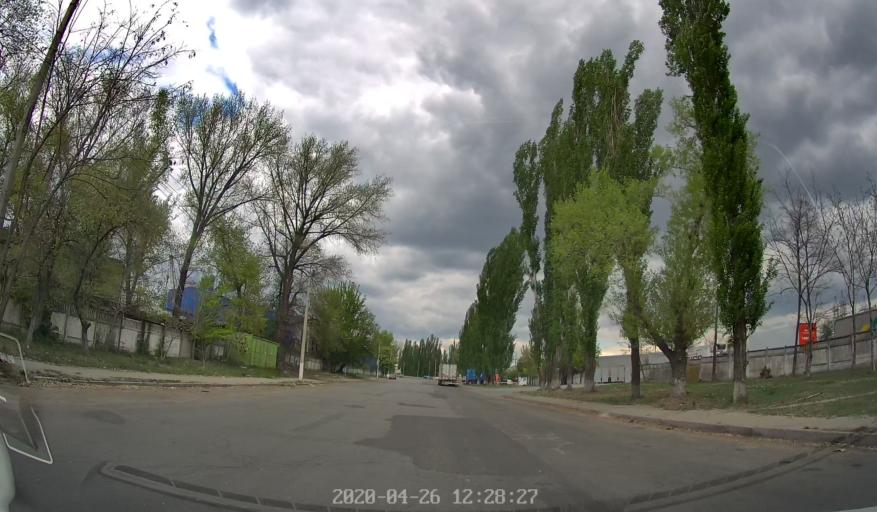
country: MD
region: Chisinau
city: Chisinau
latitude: 46.9963
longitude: 28.9071
